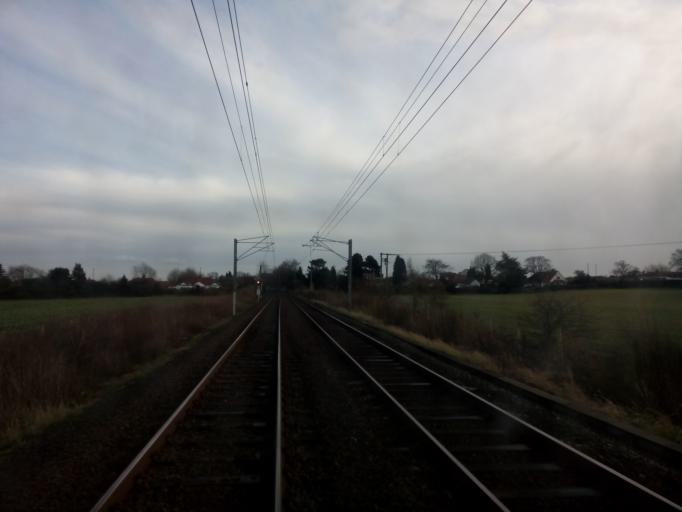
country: GB
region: England
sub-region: Newcastle upon Tyne
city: Dinnington
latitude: 55.0151
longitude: -1.6826
